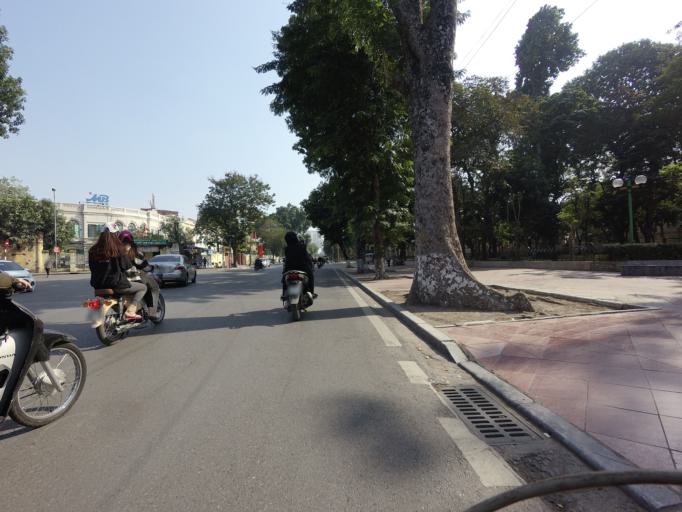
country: VN
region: Ha Noi
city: Hanoi
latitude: 21.0316
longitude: 105.8401
